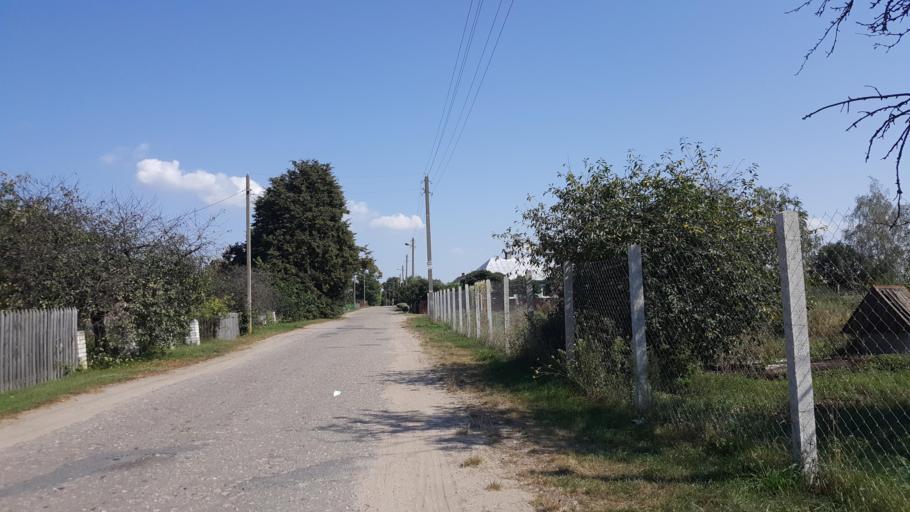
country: PL
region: Podlasie
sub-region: Powiat hajnowski
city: Czeremcha
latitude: 52.4789
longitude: 23.5420
